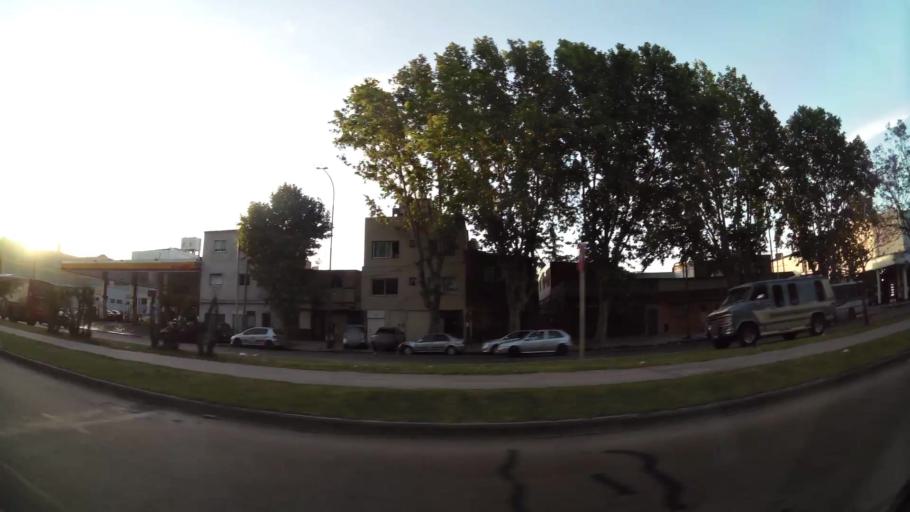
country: AR
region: Buenos Aires F.D.
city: Villa Lugano
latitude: -34.6969
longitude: -58.4686
